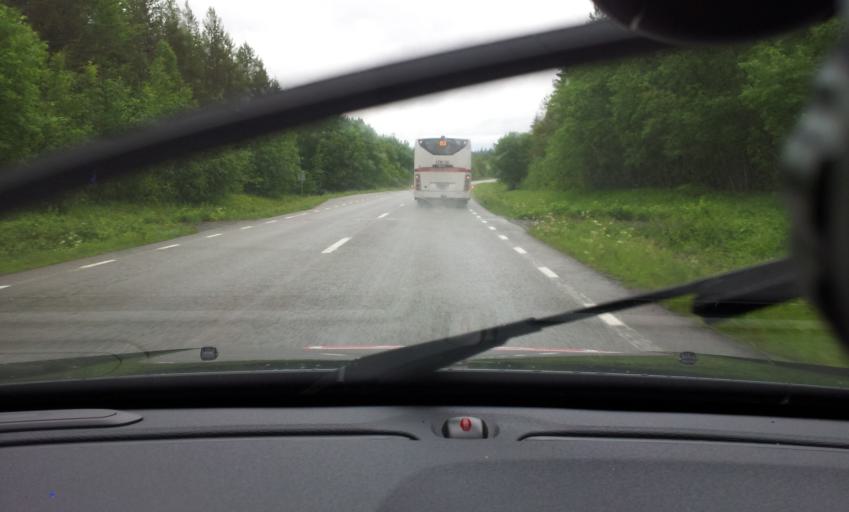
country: SE
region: Jaemtland
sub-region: OEstersunds Kommun
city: Lit
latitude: 63.5907
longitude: 14.6406
